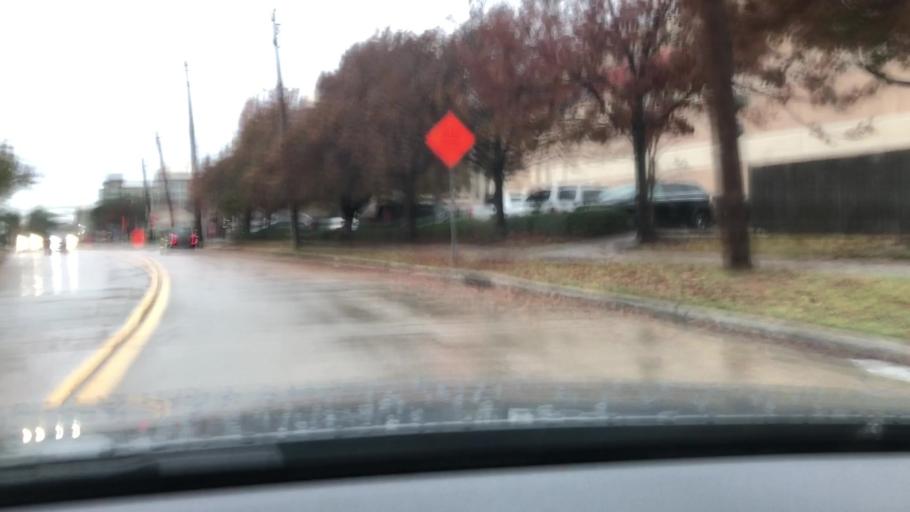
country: US
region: Texas
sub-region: Harris County
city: Bunker Hill Village
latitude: 29.7821
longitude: -95.5572
